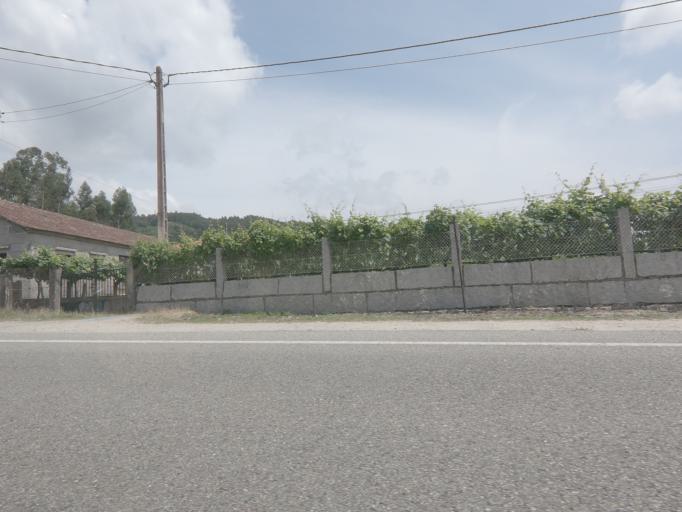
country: ES
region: Galicia
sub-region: Provincia de Pontevedra
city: Tomino
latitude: 42.0317
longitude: -8.7303
